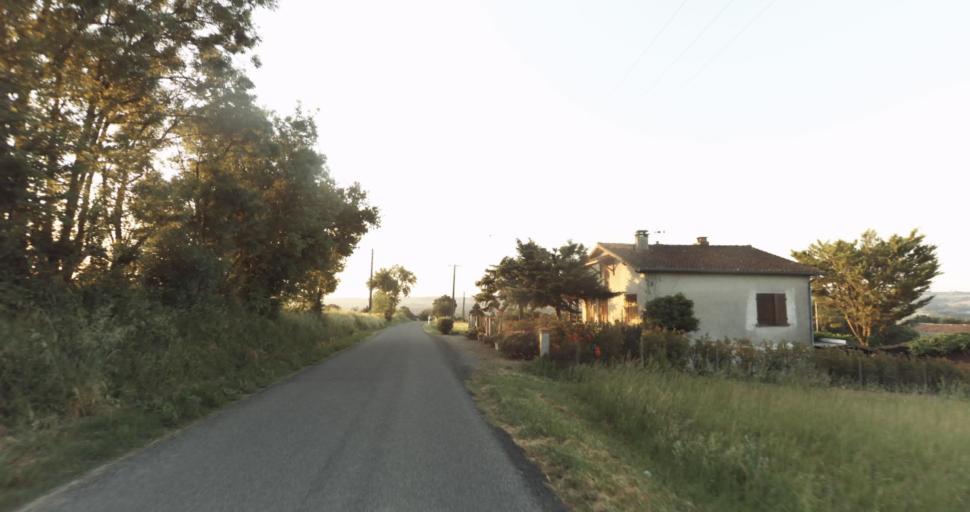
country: FR
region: Midi-Pyrenees
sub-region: Departement du Gers
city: Pujaudran
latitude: 43.6471
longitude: 1.1140
